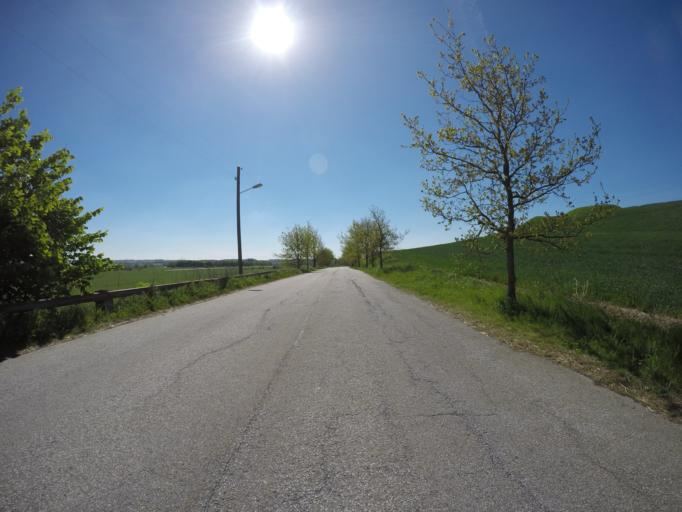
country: SE
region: Skane
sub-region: Malmo
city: Oxie
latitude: 55.5560
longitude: 13.0896
